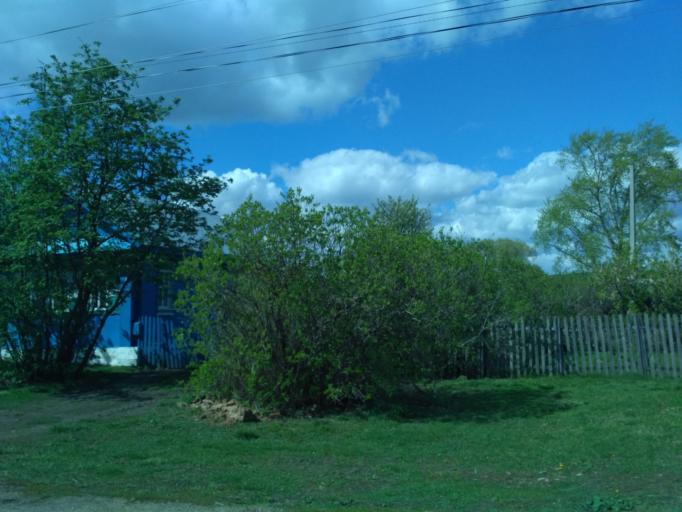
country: RU
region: Nizjnij Novgorod
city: Vad
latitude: 55.5352
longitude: 44.2070
